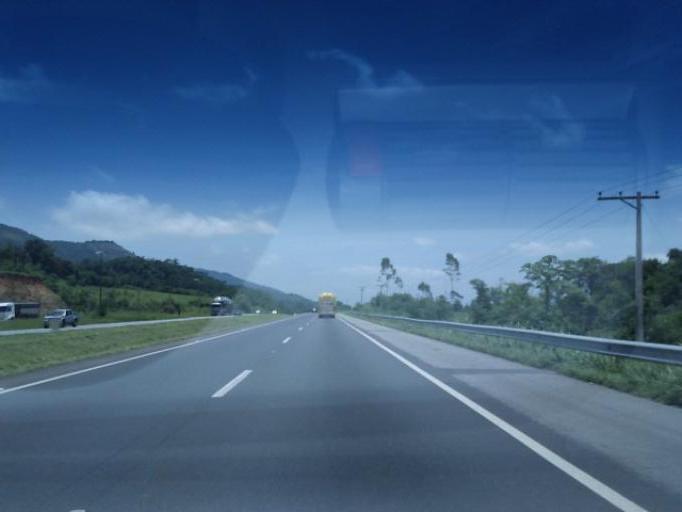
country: BR
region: Sao Paulo
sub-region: Miracatu
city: Miracatu
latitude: -24.2779
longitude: -47.4192
